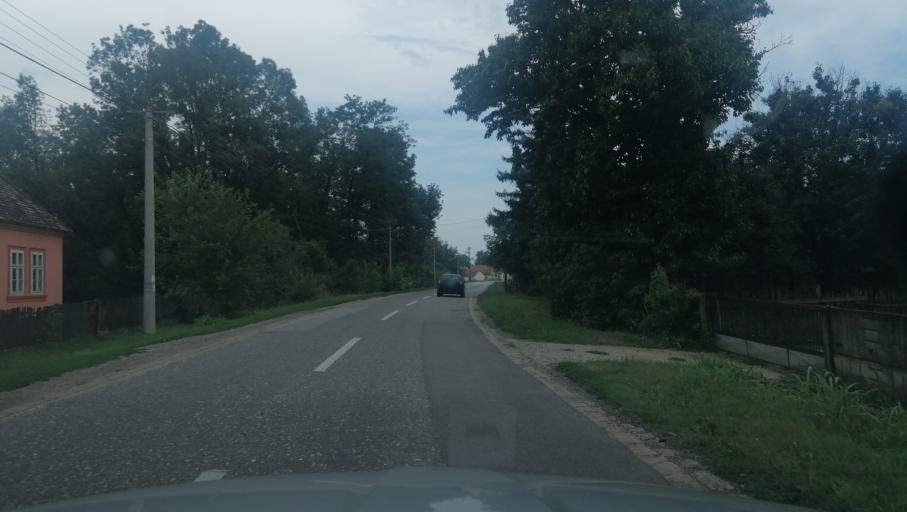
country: RS
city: Klenje
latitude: 44.8056
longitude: 19.4287
